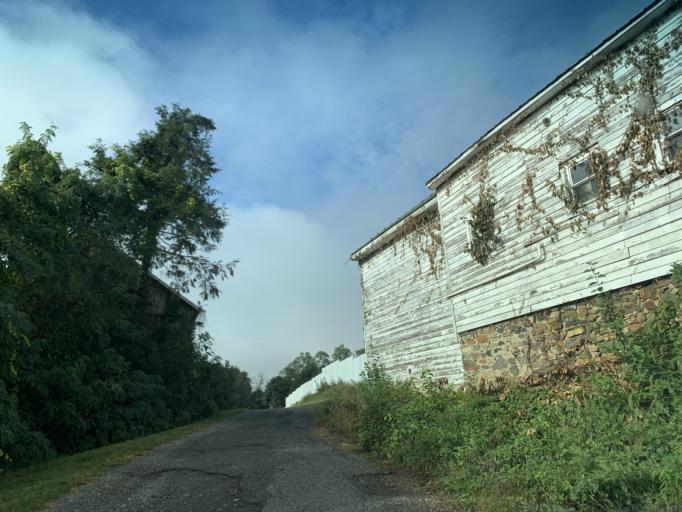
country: US
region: Maryland
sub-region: Harford County
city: Havre de Grace
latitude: 39.5616
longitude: -76.1281
